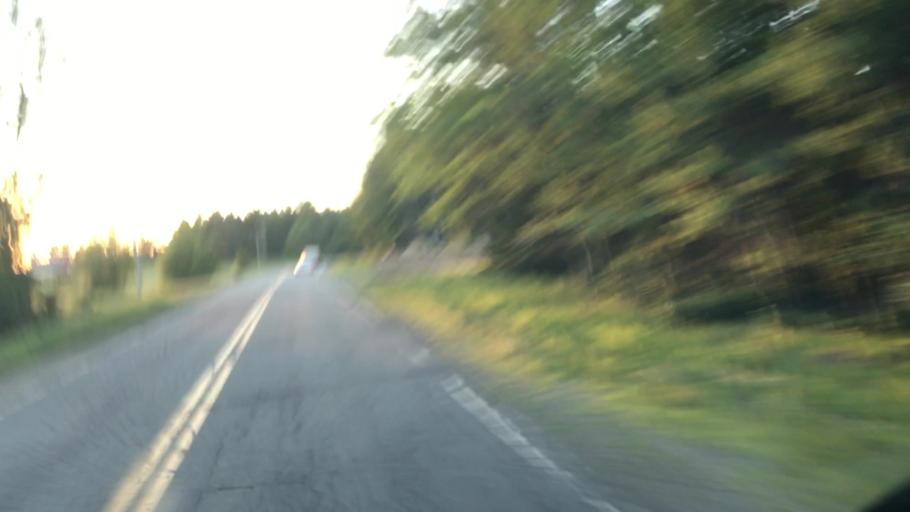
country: US
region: Maine
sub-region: Penobscot County
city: Medway
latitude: 45.6054
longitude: -68.2544
